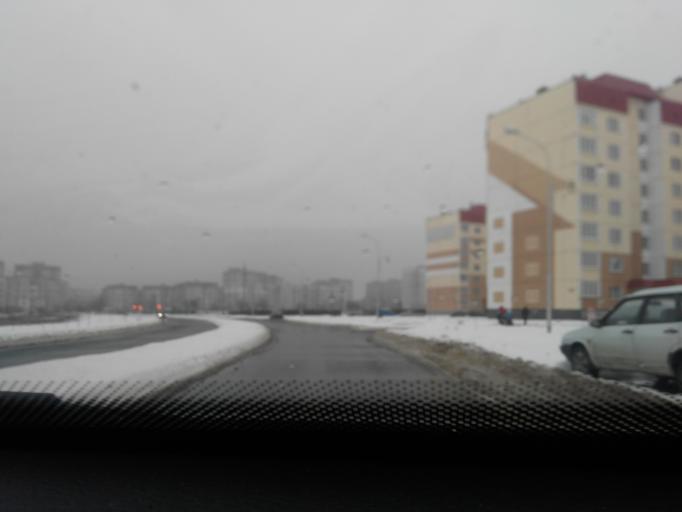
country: BY
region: Mogilev
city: Babruysk
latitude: 53.2017
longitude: 29.2232
